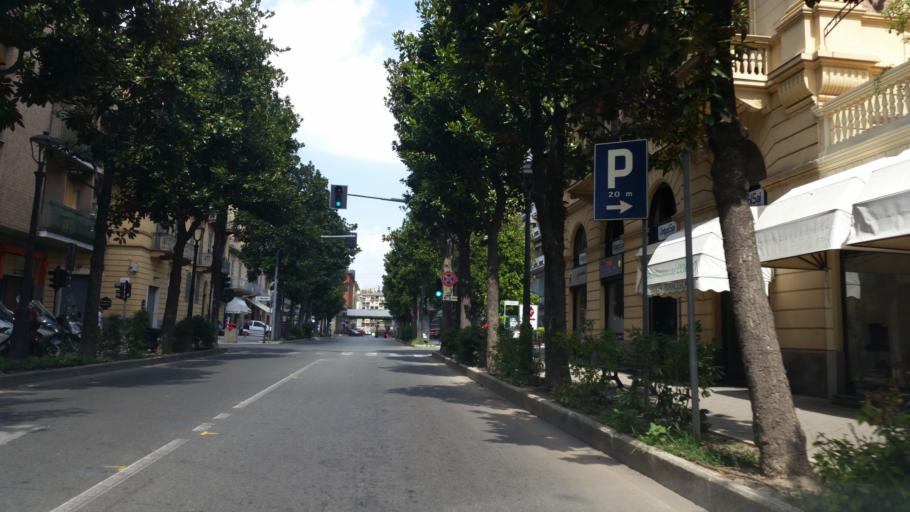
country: IT
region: Piedmont
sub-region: Provincia di Alessandria
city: Acqui Terme
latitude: 44.6707
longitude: 8.4687
